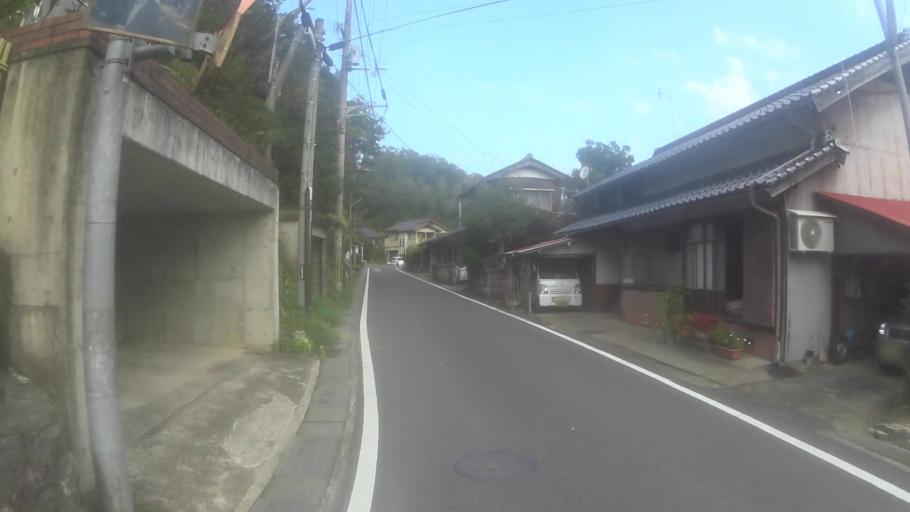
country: JP
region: Kyoto
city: Miyazu
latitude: 35.5706
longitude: 135.1160
